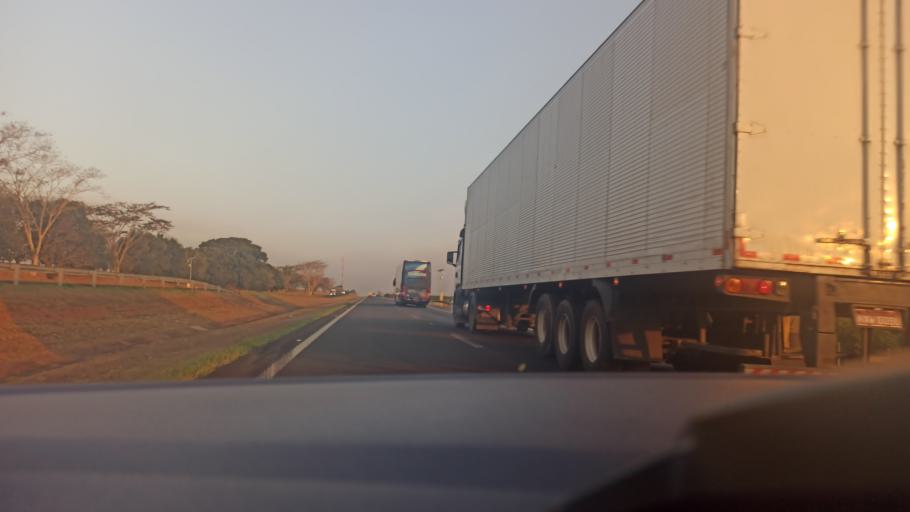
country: BR
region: Sao Paulo
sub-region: Santa Adelia
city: Santa Adelia
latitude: -21.4030
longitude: -48.7034
